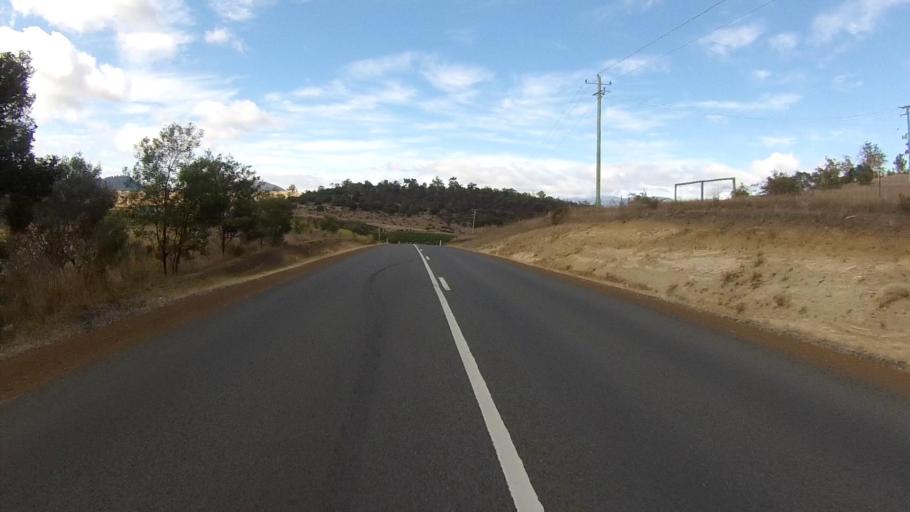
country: AU
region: Tasmania
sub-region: Brighton
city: Old Beach
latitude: -42.7392
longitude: 147.2882
